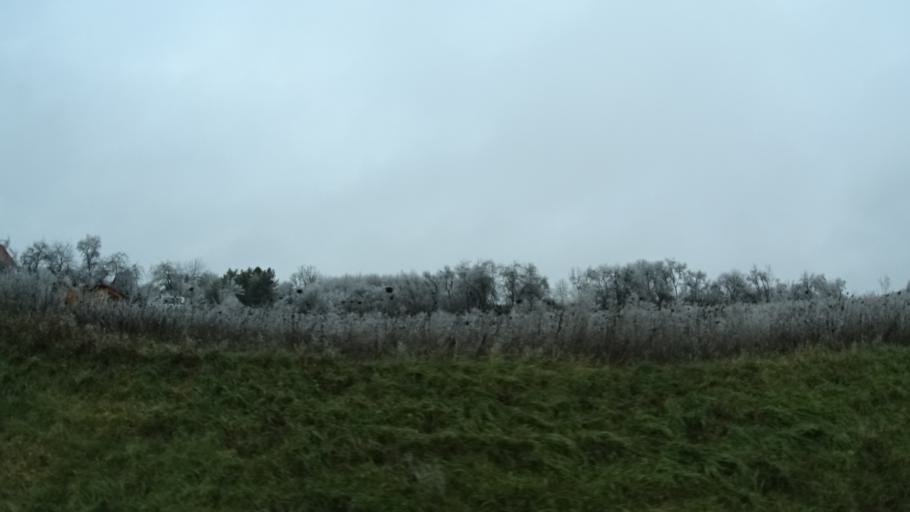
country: DE
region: Baden-Wuerttemberg
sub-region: Regierungsbezirk Stuttgart
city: Igersheim
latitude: 49.5409
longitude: 9.7994
